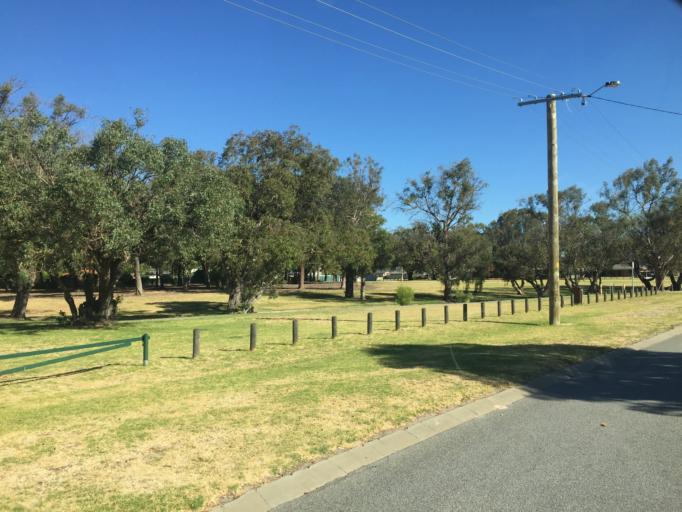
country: AU
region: Western Australia
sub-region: Canning
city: East Cannington
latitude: -32.0143
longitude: 115.9689
